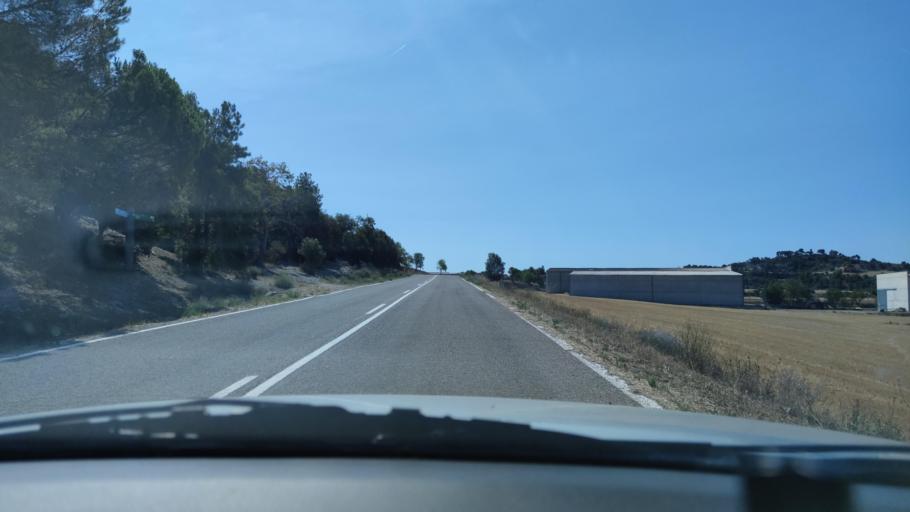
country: ES
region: Catalonia
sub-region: Provincia de Lleida
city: Sant Guim de Freixenet
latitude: 41.6247
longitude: 1.3476
